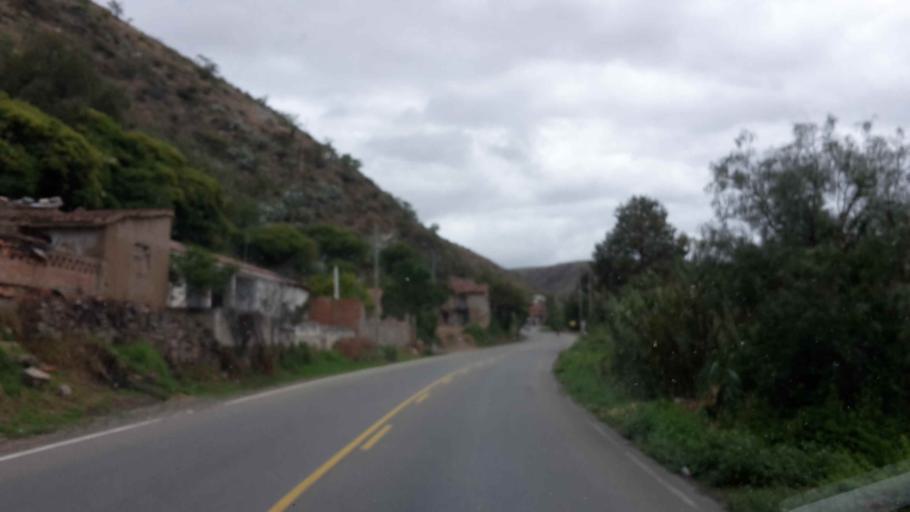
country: BO
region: Cochabamba
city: Punata
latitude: -17.5111
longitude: -65.8102
